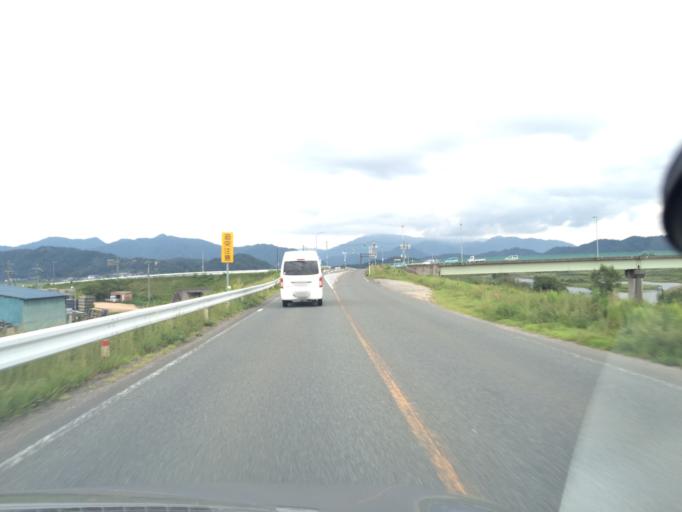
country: JP
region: Hyogo
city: Toyooka
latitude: 35.5085
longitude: 134.8327
